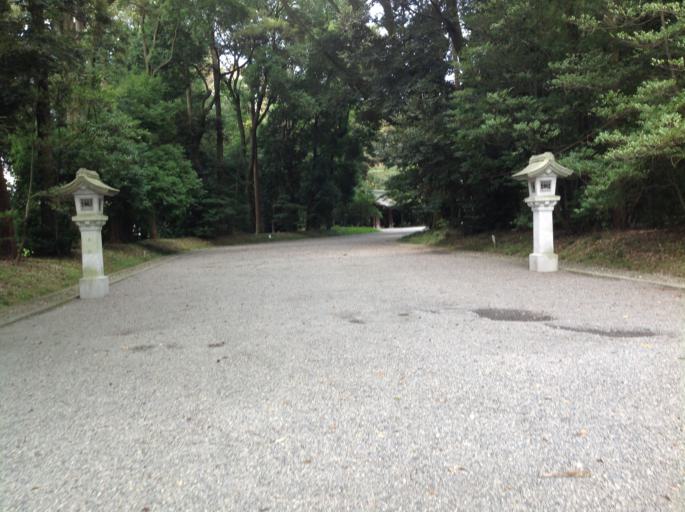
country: JP
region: Tochigi
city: Utsunomiya-shi
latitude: 36.5706
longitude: 139.8604
